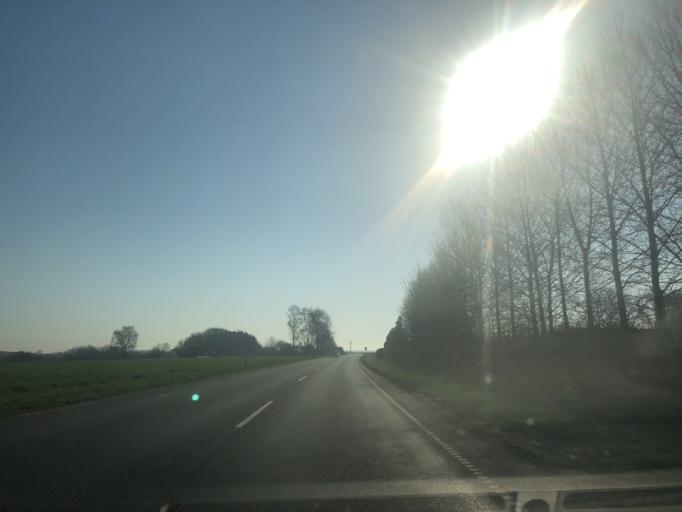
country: DK
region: Zealand
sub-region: Faxe Kommune
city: Fakse
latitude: 55.2707
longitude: 12.1241
